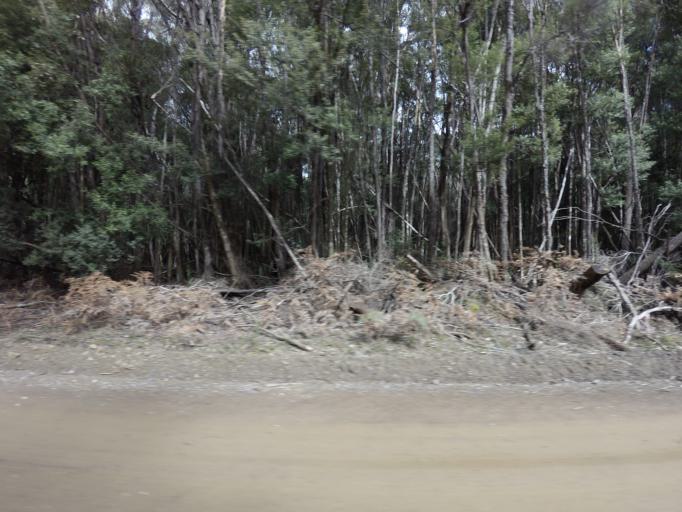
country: AU
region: Tasmania
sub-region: Huon Valley
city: Geeveston
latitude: -43.4055
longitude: 146.8676
